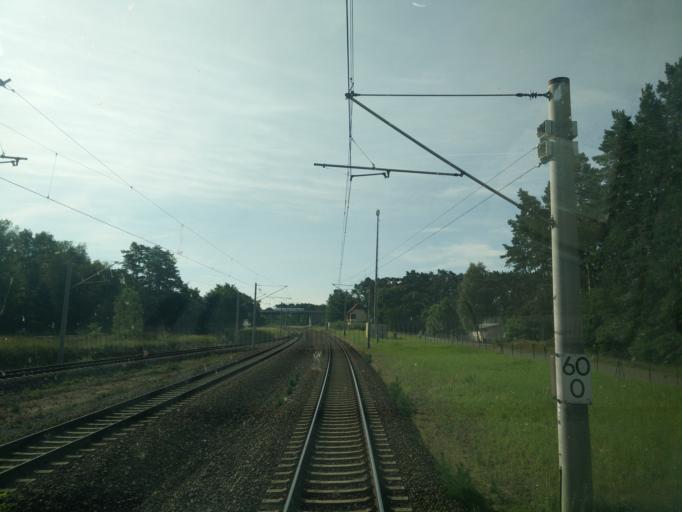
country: DE
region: Brandenburg
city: Halbe
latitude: 52.0281
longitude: 13.7227
